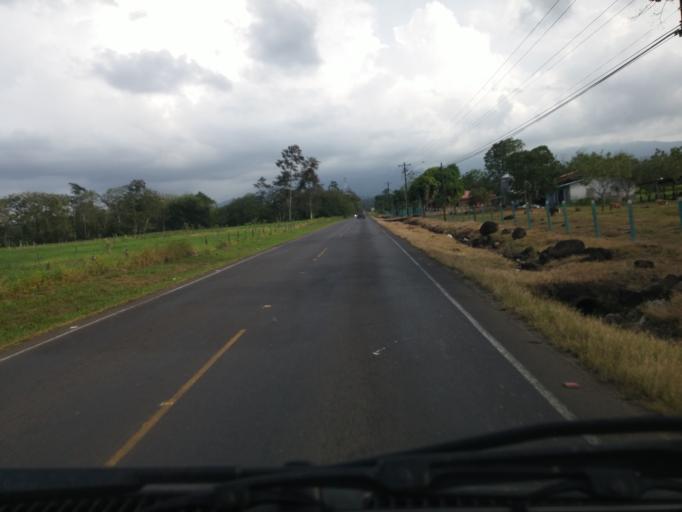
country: CR
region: Alajuela
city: Pital
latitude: 10.4232
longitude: -84.3390
